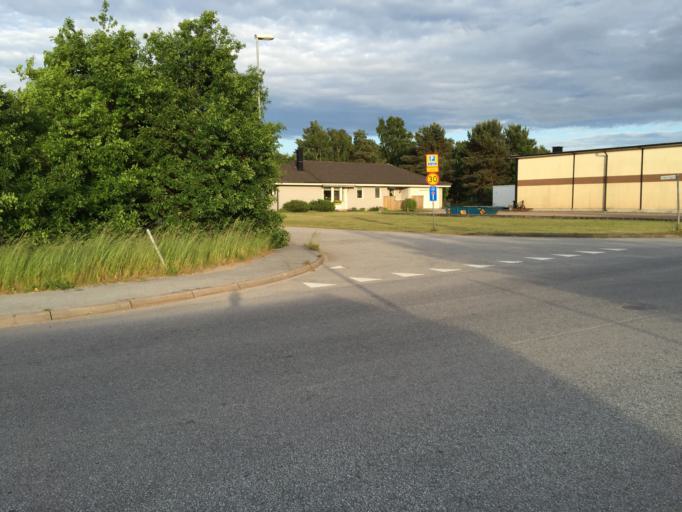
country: SE
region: Skane
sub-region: Lunds Kommun
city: Veberod
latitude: 55.6394
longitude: 13.5023
